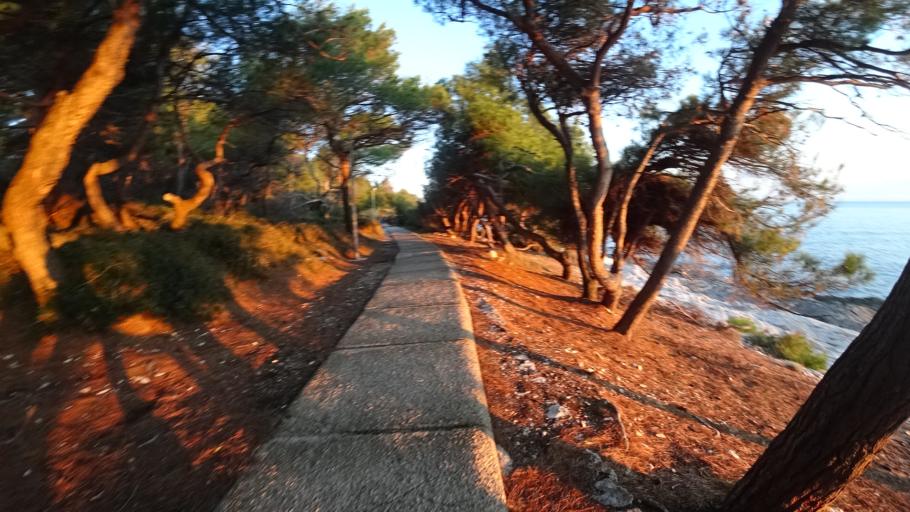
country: HR
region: Primorsko-Goranska
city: Mali Losinj
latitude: 44.5247
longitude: 14.4493
